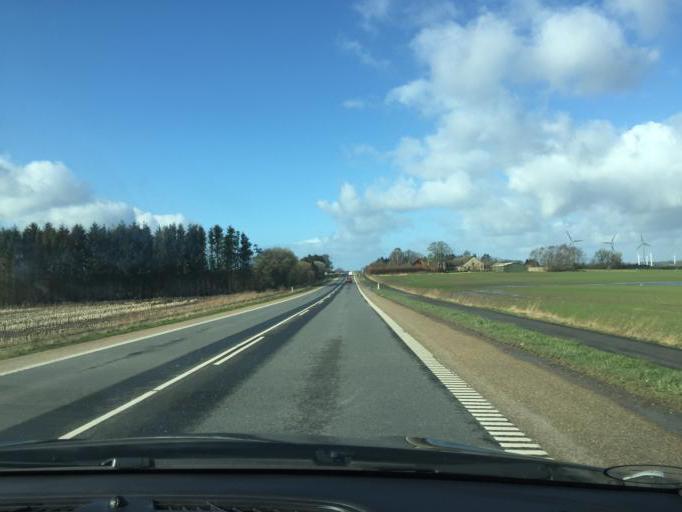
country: DK
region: South Denmark
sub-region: Middelfart Kommune
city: Norre Aby
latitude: 55.4806
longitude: 9.8434
